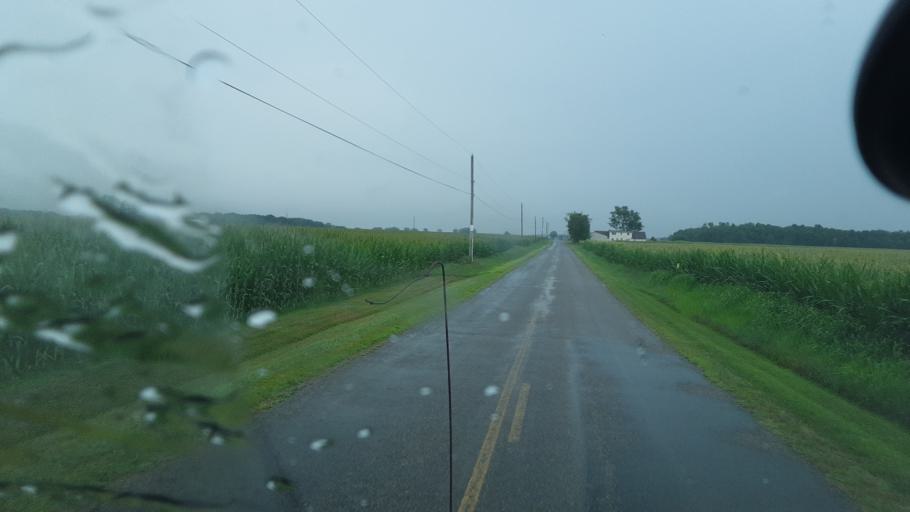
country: US
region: Ohio
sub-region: Williams County
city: Edgerton
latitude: 41.5014
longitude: -84.7880
